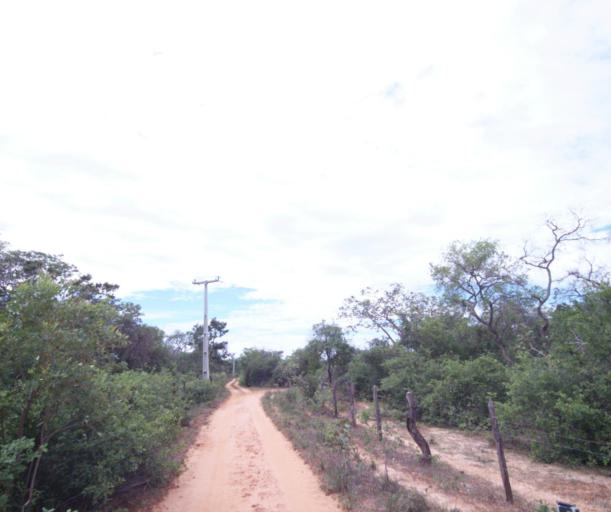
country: BR
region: Bahia
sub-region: Carinhanha
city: Carinhanha
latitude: -14.2409
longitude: -44.3818
